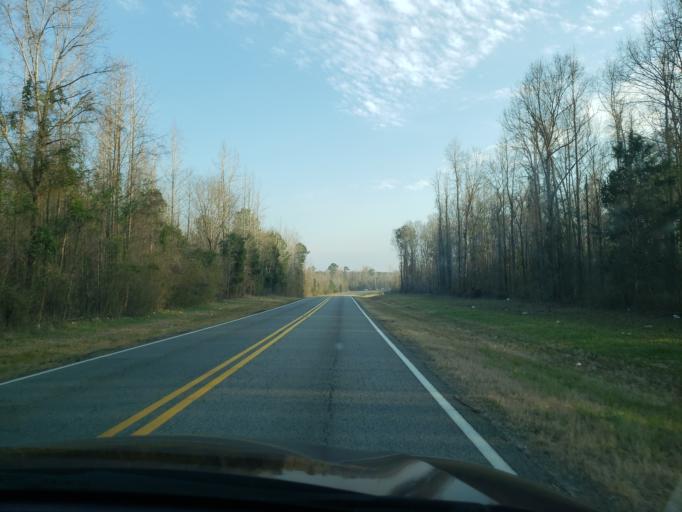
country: US
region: Alabama
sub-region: Hale County
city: Greensboro
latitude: 32.7774
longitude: -87.5867
